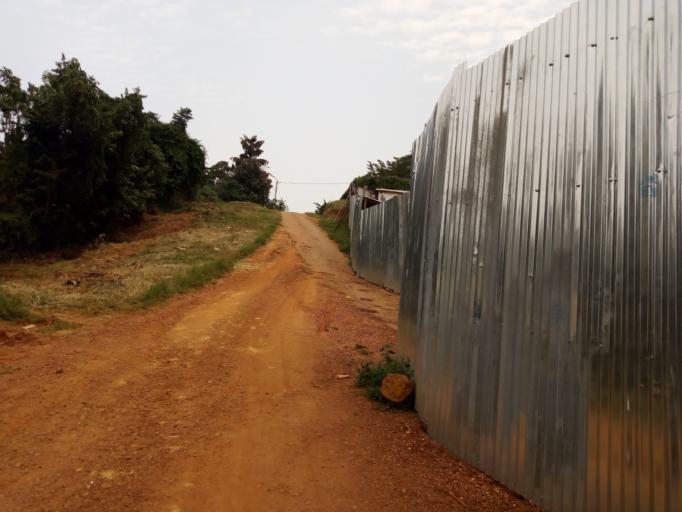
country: UG
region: Central Region
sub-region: Wakiso District
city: Kireka
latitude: 0.3282
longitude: 32.6330
